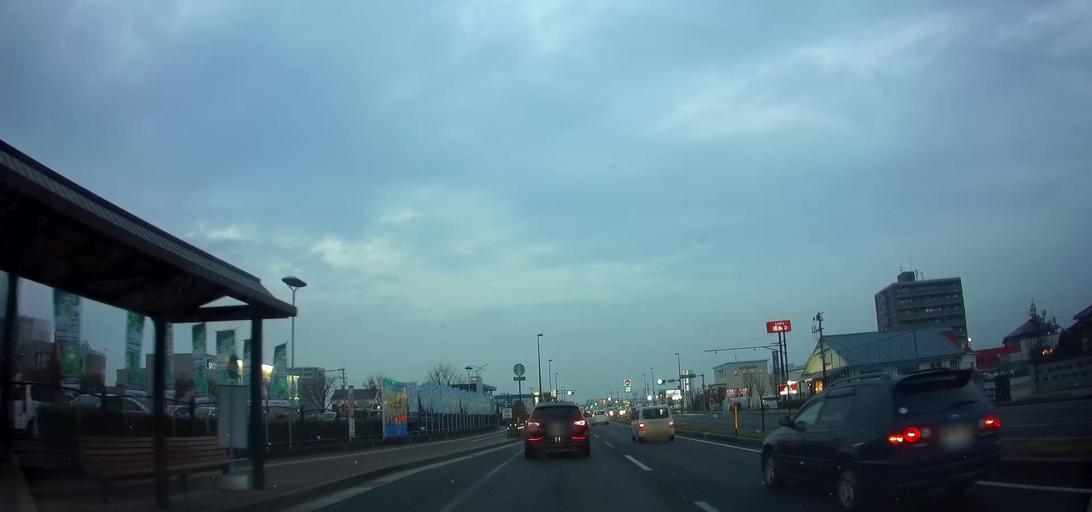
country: JP
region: Nagasaki
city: Omura
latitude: 32.9006
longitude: 129.9587
